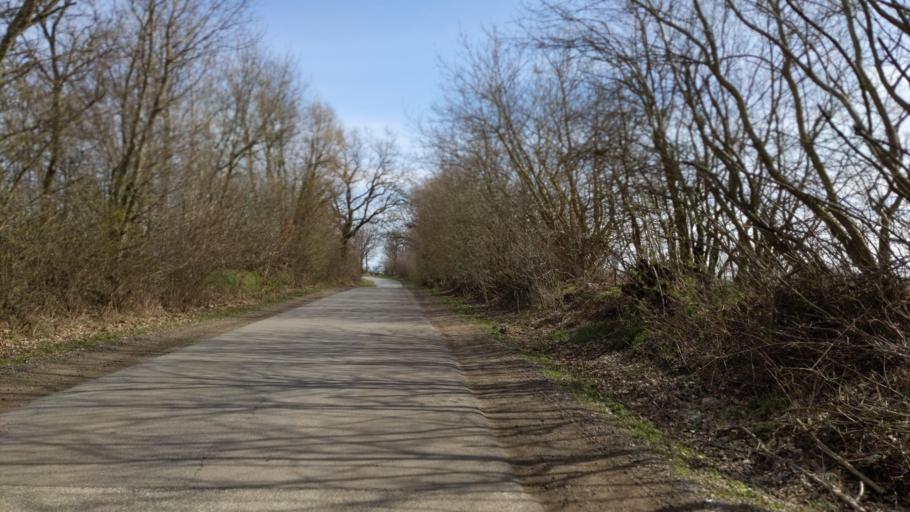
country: DE
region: Schleswig-Holstein
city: Susel
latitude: 54.0713
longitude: 10.6745
